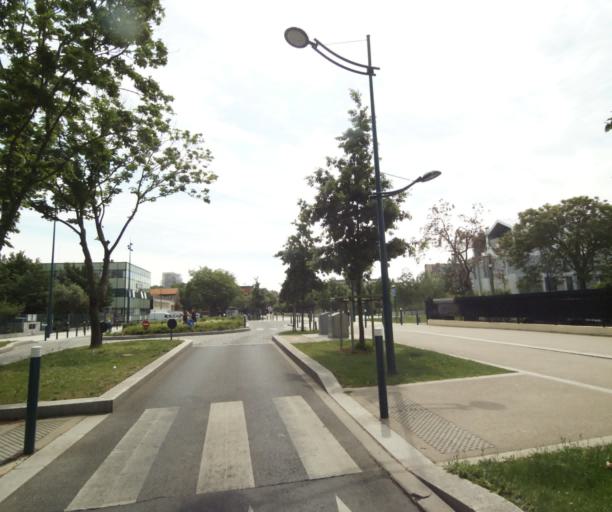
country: FR
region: Ile-de-France
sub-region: Departement des Hauts-de-Seine
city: Gennevilliers
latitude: 48.9189
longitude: 2.2993
